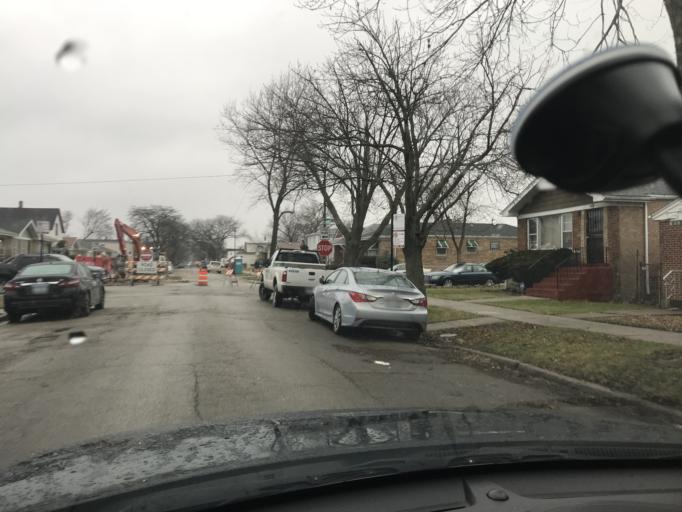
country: US
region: Illinois
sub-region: Cook County
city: Evergreen Park
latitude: 41.7248
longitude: -87.6360
